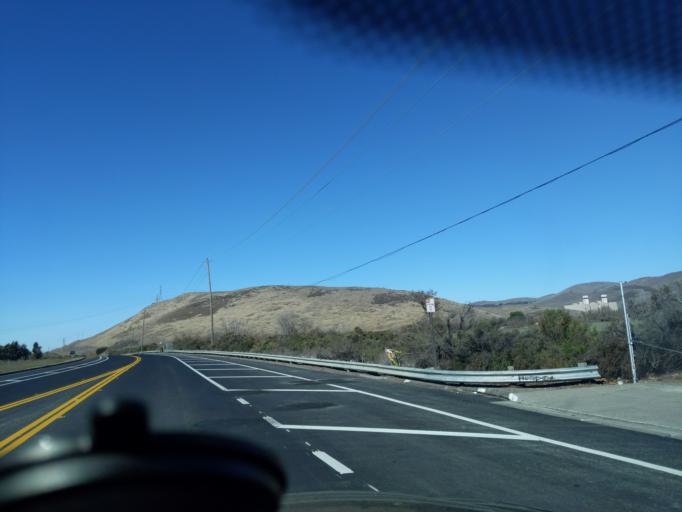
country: US
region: California
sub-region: Santa Clara County
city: Seven Trees
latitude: 37.2098
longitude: -121.7458
